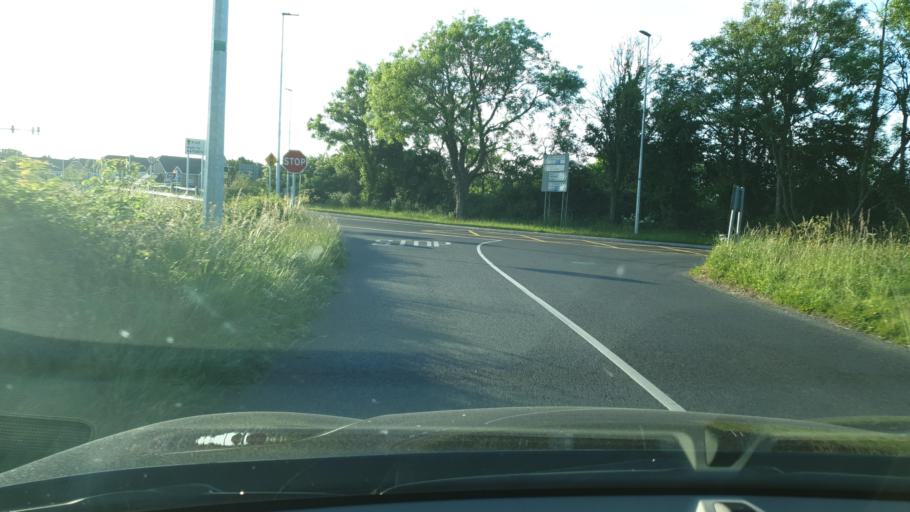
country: IE
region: Leinster
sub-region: An Mhi
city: Ratoath
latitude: 53.5032
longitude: -6.4443
